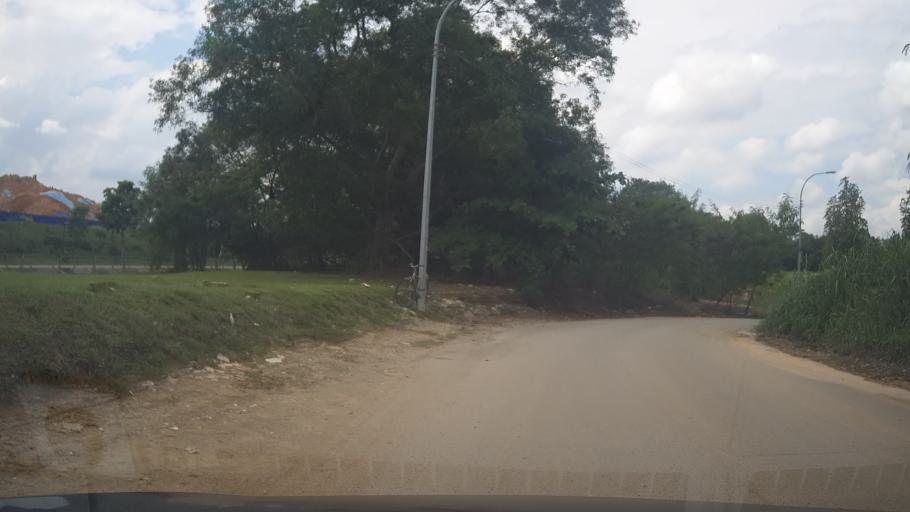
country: MY
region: Johor
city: Kampung Pasir Gudang Baru
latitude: 1.3848
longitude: 103.9349
